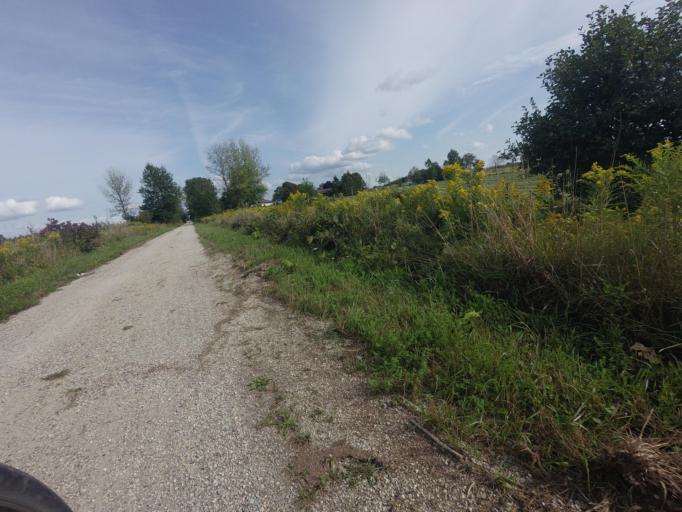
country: CA
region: Ontario
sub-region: Wellington County
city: Guelph
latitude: 43.5802
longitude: -80.3944
